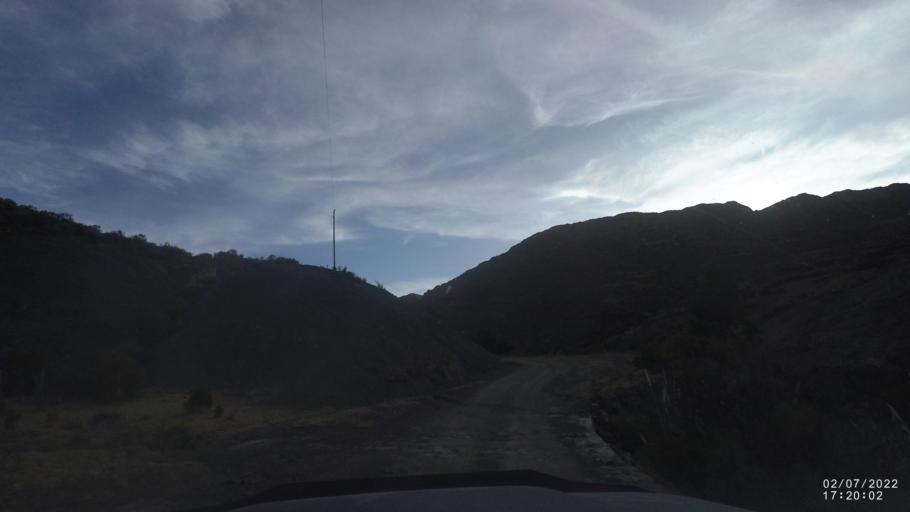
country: BO
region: Cochabamba
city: Irpa Irpa
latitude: -17.8761
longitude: -66.5935
